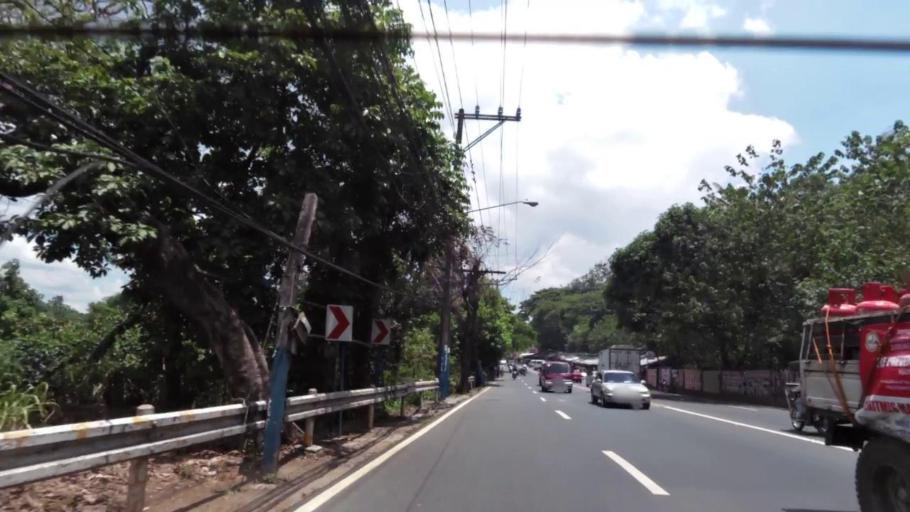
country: PH
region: Calabarzon
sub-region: Province of Rizal
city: Cainta
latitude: 14.5999
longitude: 121.1738
